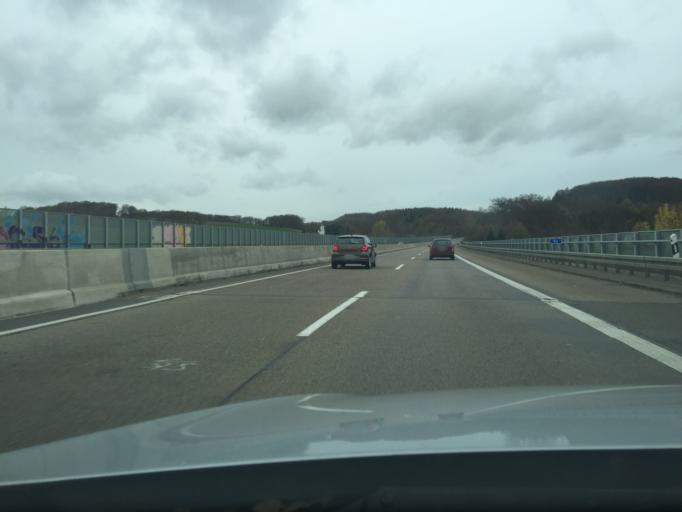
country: DE
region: North Rhine-Westphalia
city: Wulfrath
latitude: 51.2792
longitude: 7.0761
